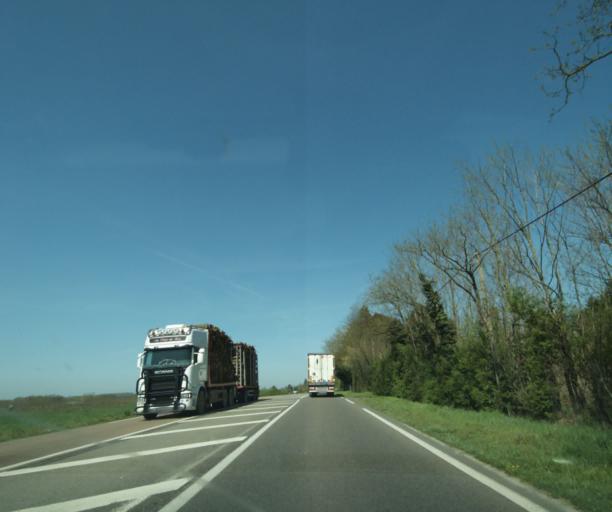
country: FR
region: Bourgogne
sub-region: Departement de la Nievre
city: Chantenay-Saint-Imbert
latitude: 46.7392
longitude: 3.1614
